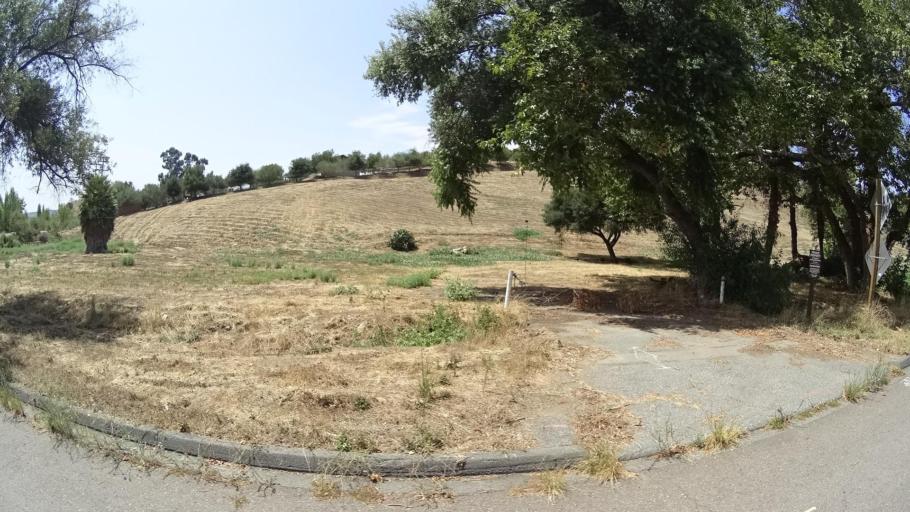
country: US
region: California
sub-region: San Diego County
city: Bonsall
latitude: 33.3034
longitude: -117.2157
